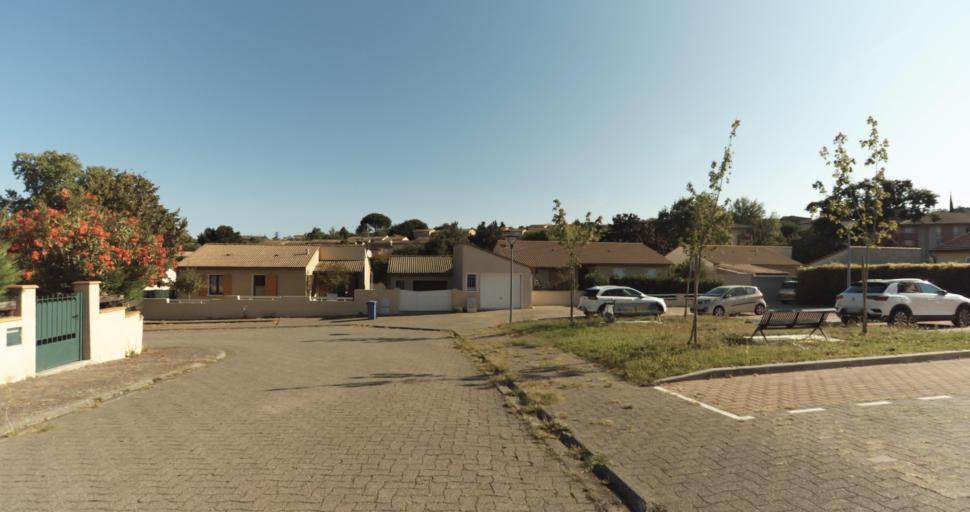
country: FR
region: Midi-Pyrenees
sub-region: Departement de la Haute-Garonne
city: L'Union
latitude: 43.6637
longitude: 1.4790
